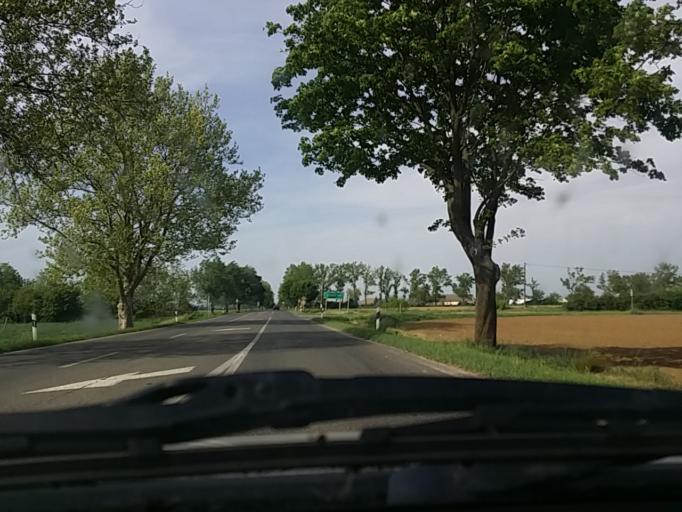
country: HU
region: Baranya
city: Harkany
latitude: 45.9173
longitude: 18.2327
